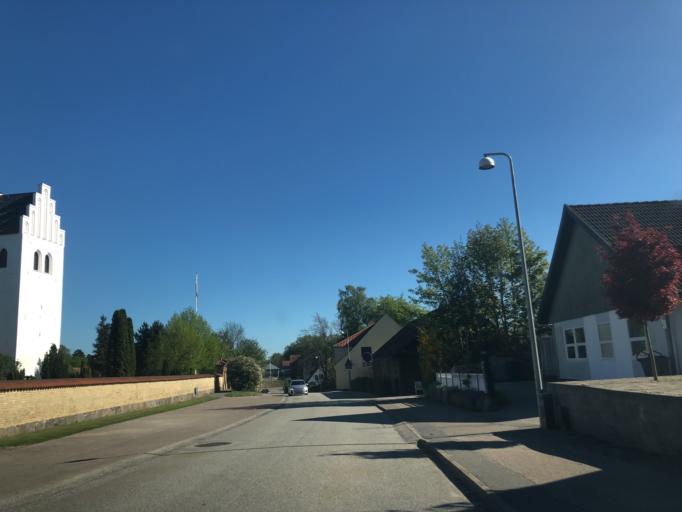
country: DK
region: Zealand
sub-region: Koge Kommune
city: Koge
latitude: 55.4180
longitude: 12.1473
